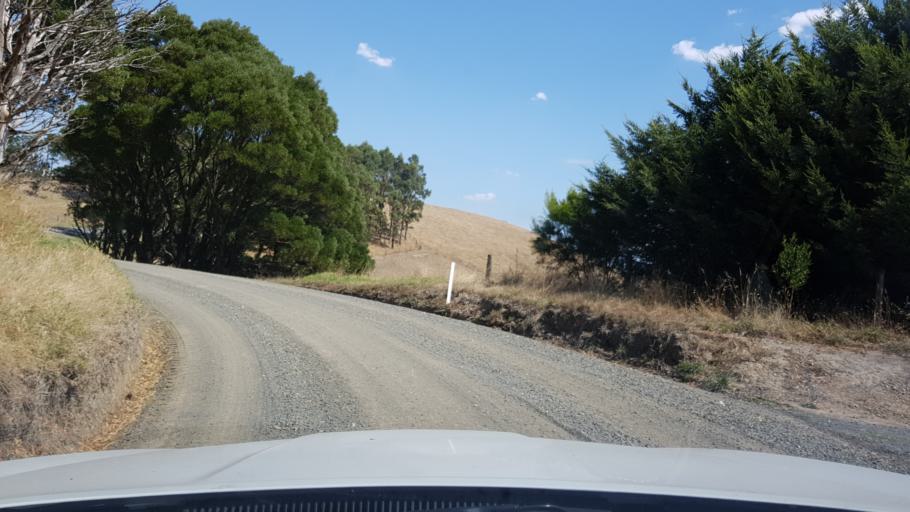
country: AU
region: Victoria
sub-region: Baw Baw
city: Warragul
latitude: -38.2868
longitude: 145.9179
